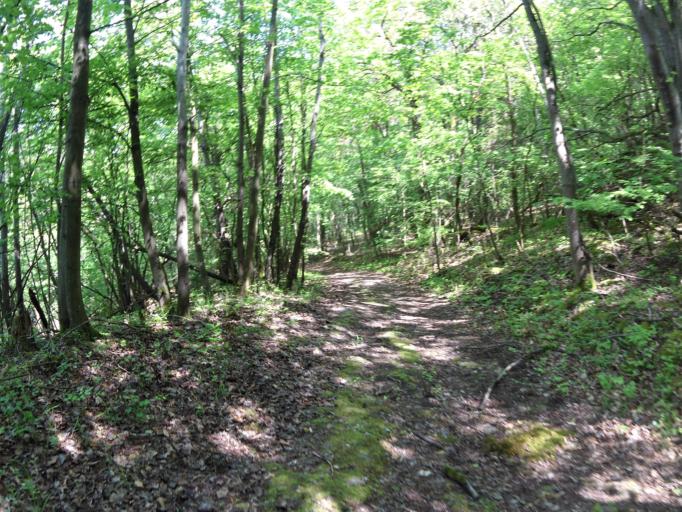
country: DE
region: Bavaria
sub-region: Regierungsbezirk Unterfranken
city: Eibelstadt
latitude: 49.7393
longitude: 10.0129
